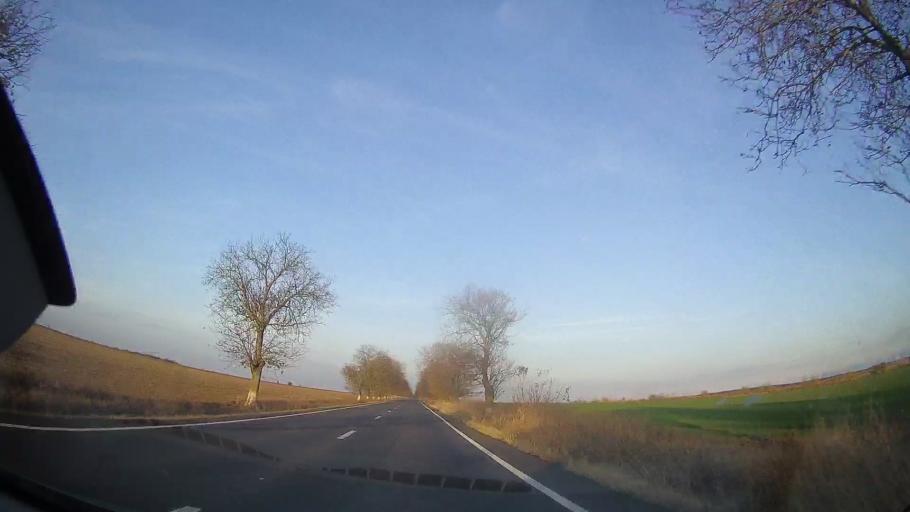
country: RO
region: Constanta
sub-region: Comuna Amzacea
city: Amzacea
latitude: 43.9477
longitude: 28.3789
